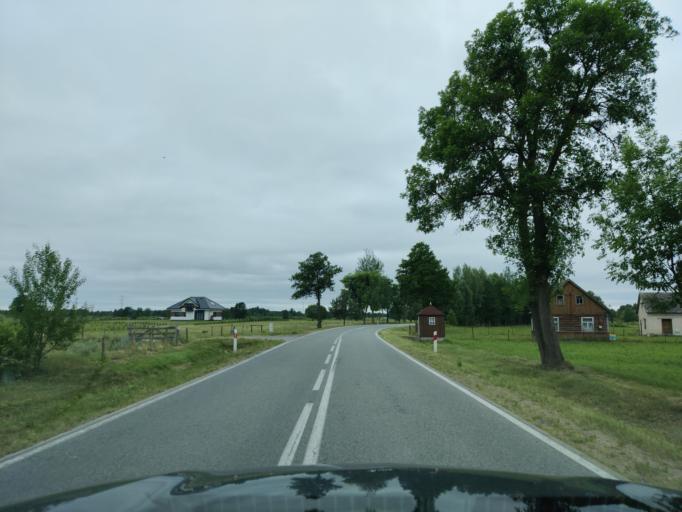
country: PL
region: Masovian Voivodeship
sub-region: Powiat ostrolecki
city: Czarnia
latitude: 53.3255
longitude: 21.1693
